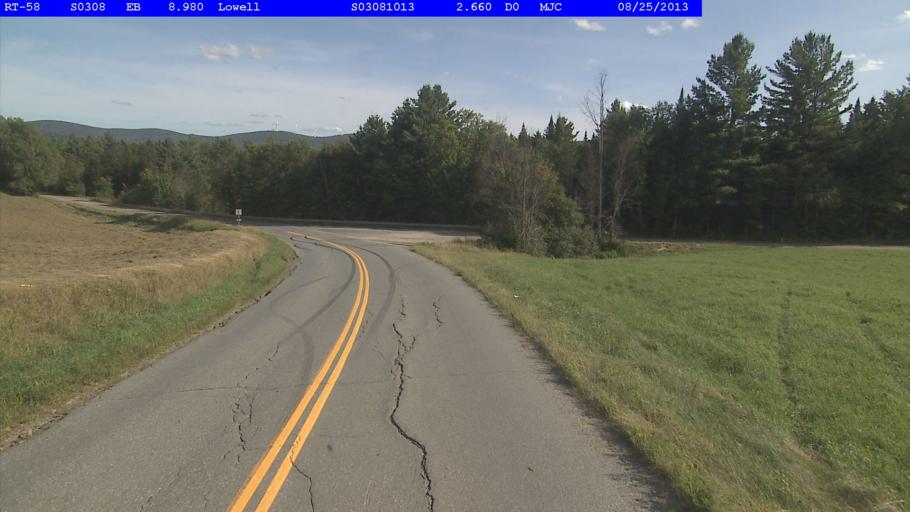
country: US
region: Vermont
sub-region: Lamoille County
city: Hyde Park
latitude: 44.8127
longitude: -72.4668
